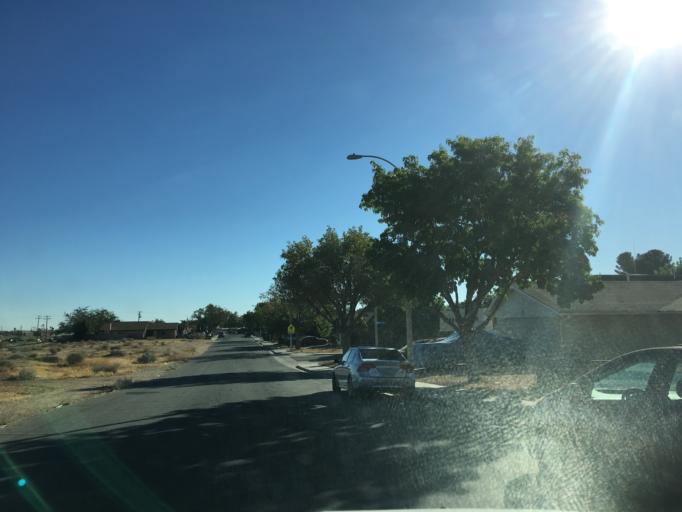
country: US
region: California
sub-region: Los Angeles County
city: Desert View Highlands
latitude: 34.5920
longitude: -118.1573
